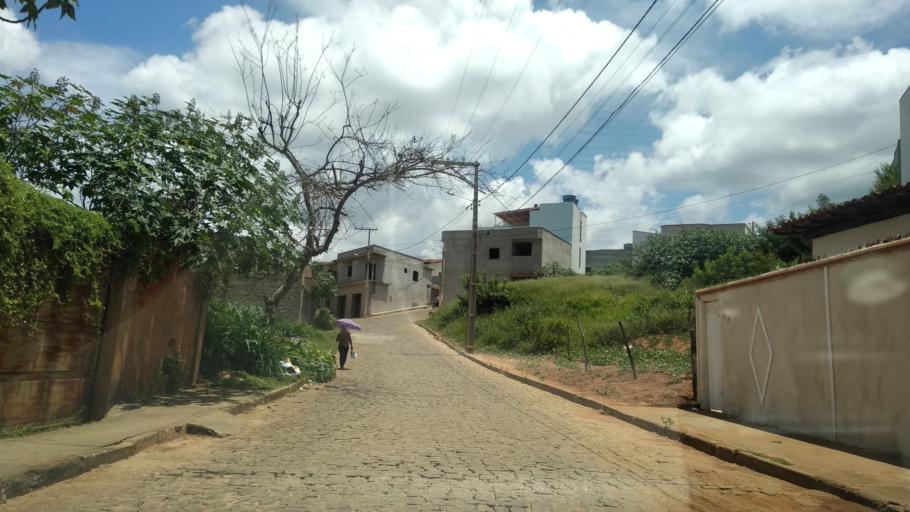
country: BR
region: Bahia
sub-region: Caetite
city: Caetite
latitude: -14.0617
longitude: -42.4890
